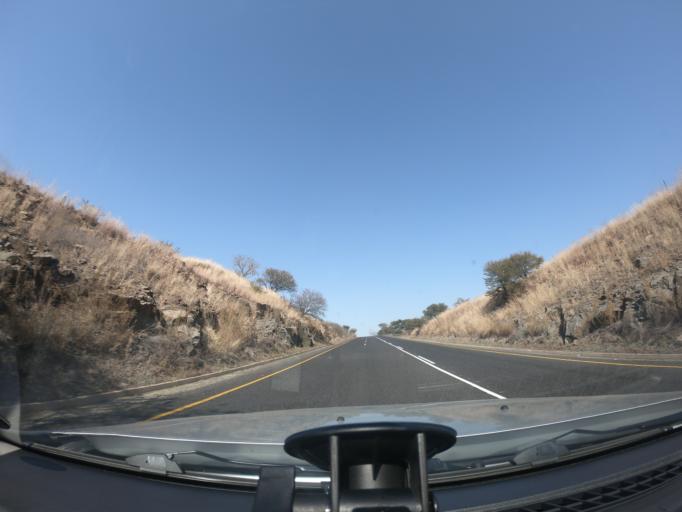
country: ZA
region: KwaZulu-Natal
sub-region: uThukela District Municipality
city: Ladysmith
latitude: -28.6871
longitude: 29.8265
